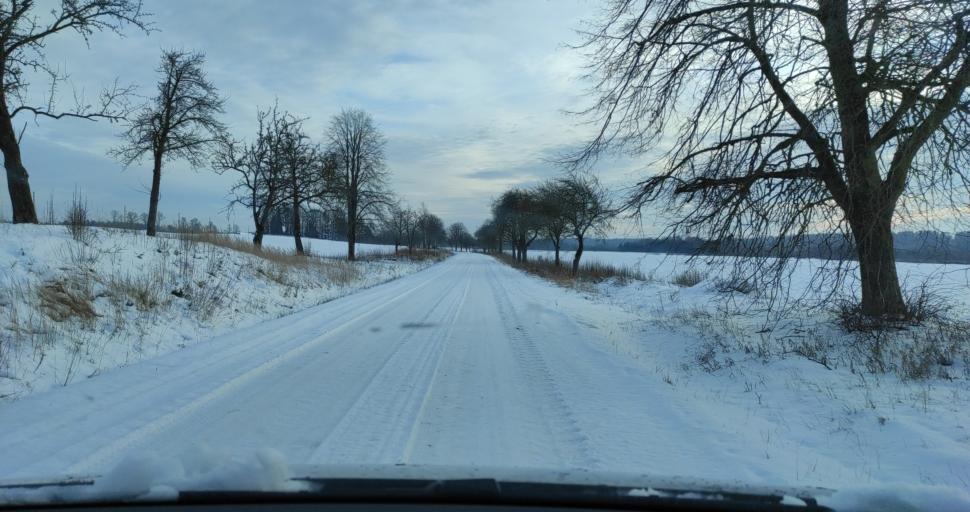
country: LV
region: Kuldigas Rajons
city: Kuldiga
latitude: 56.9528
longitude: 22.0167
